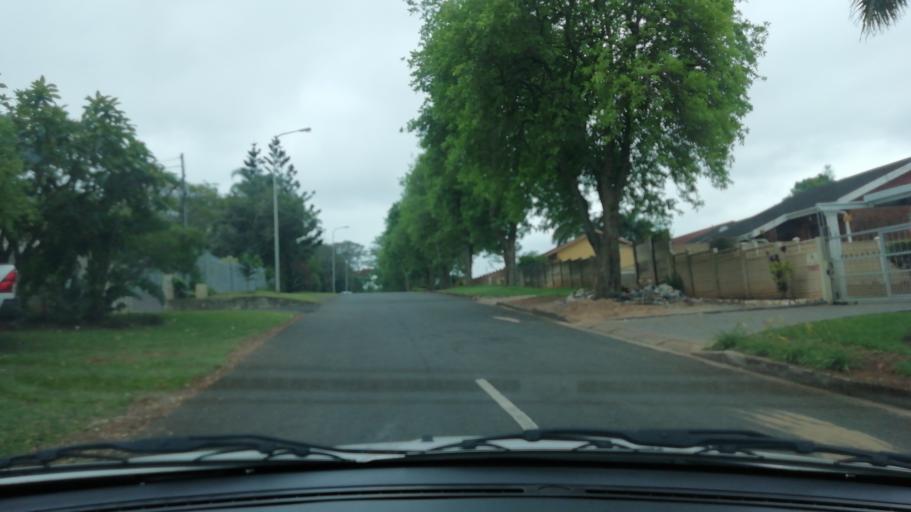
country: ZA
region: KwaZulu-Natal
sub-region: uThungulu District Municipality
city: Empangeni
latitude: -28.7676
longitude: 31.8913
